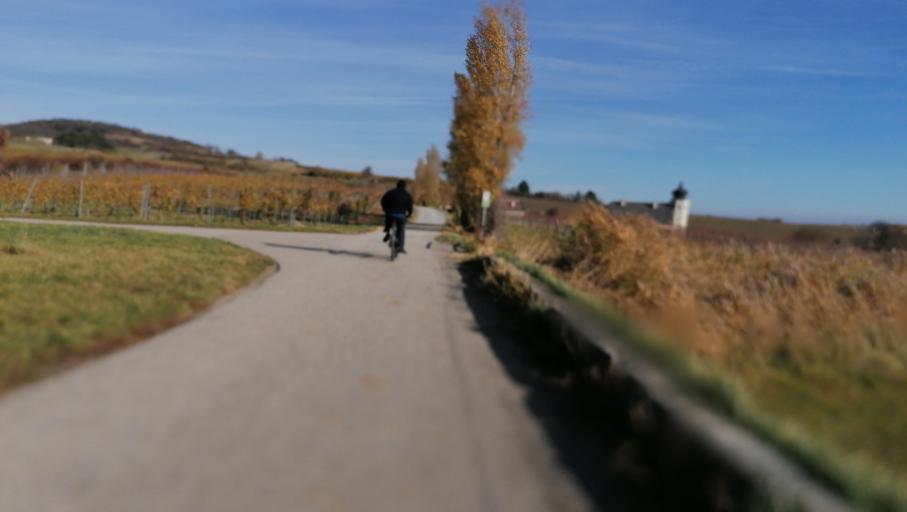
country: AT
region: Lower Austria
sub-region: Politischer Bezirk Modling
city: Gumpoldskirchen
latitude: 48.0503
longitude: 16.2895
